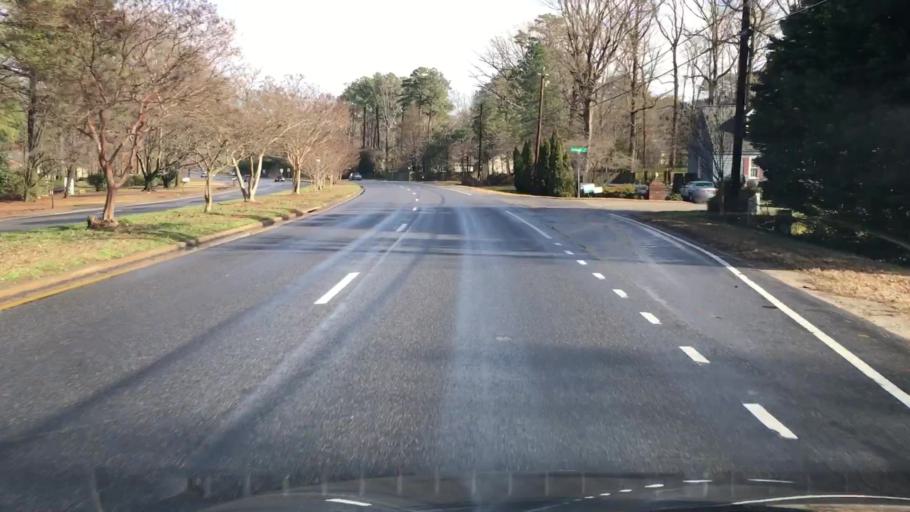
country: US
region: Virginia
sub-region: Chesterfield County
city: Bon Air
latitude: 37.5321
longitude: -77.5799
